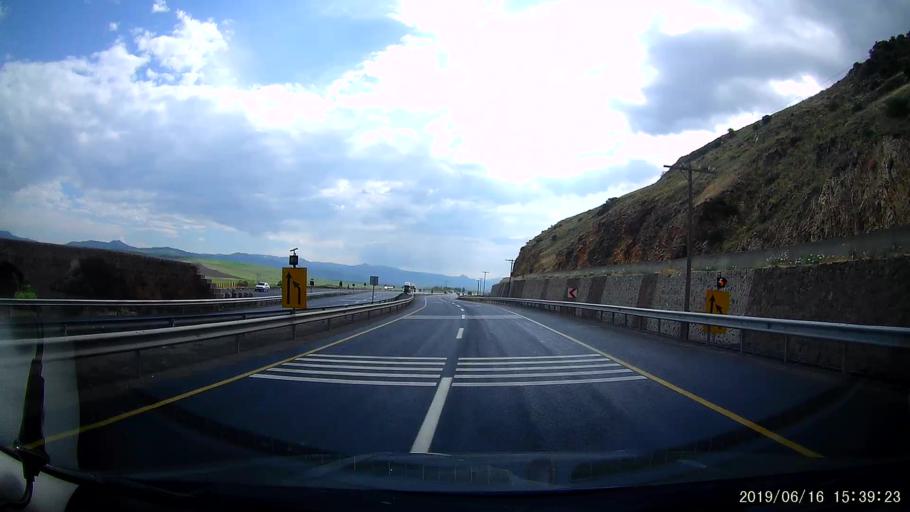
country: TR
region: Erzurum
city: Koprukoy
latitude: 39.9709
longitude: 41.8881
